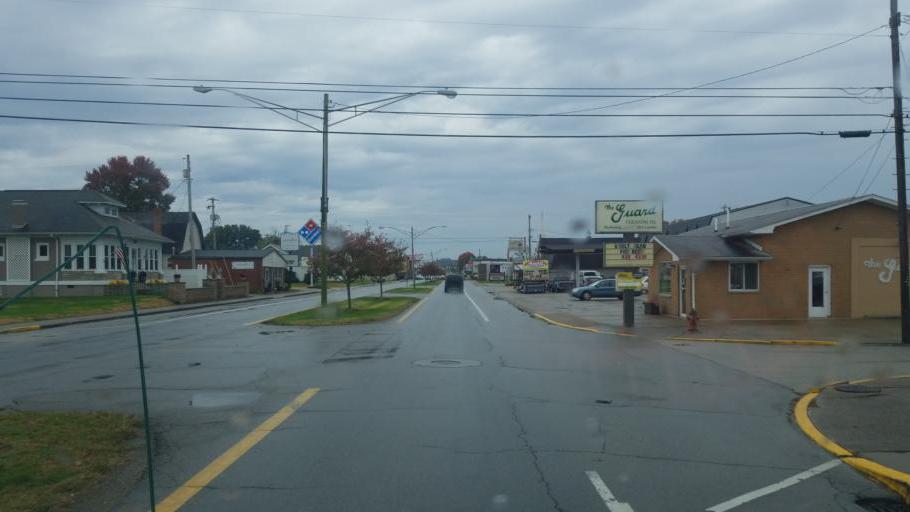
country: US
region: West Virginia
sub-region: Wood County
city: Vienna
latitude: 39.3272
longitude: -81.5486
